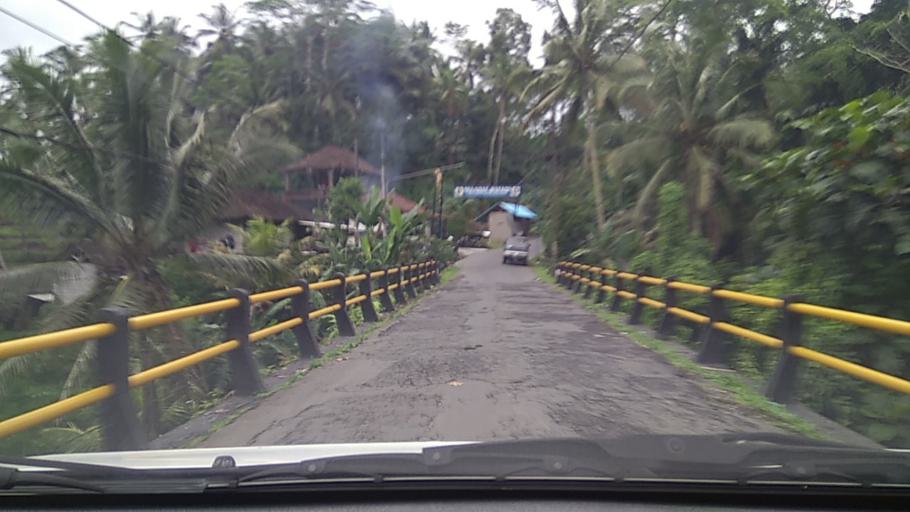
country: ID
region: Bali
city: Banjar Manukayaanyar
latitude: -8.4197
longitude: 115.3030
